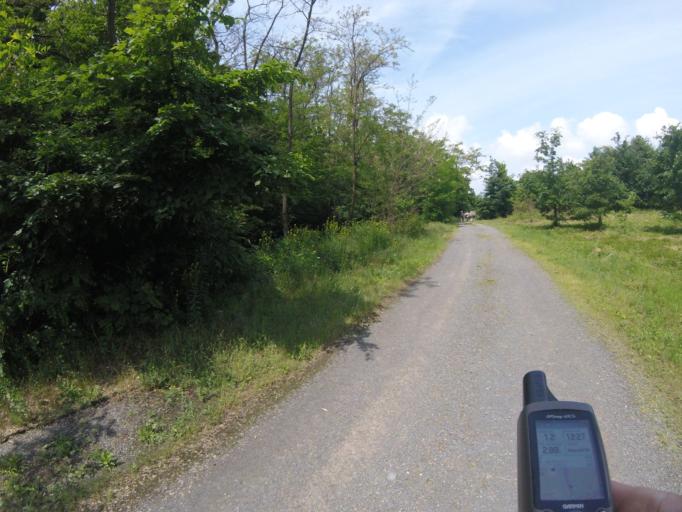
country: HU
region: Zala
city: Turje
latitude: 46.9111
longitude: 17.1822
